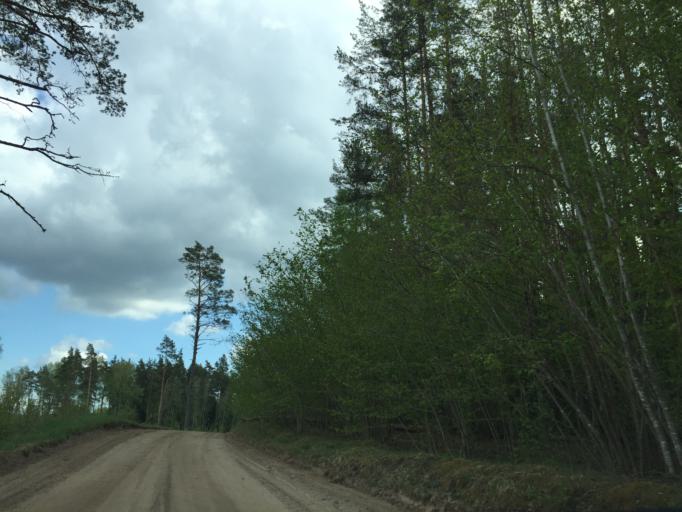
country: LV
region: Pargaujas
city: Stalbe
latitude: 57.3150
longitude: 24.8780
